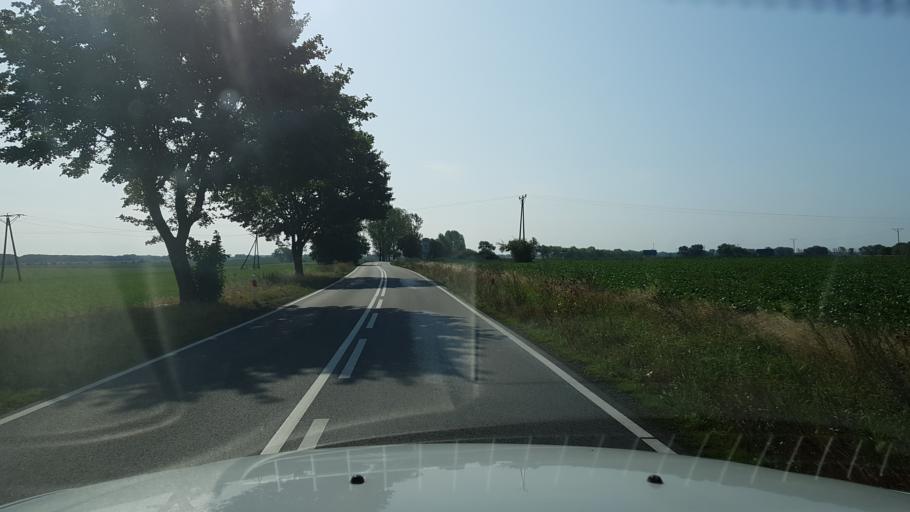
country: PL
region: West Pomeranian Voivodeship
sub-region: Powiat stargardzki
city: Stargard Szczecinski
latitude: 53.2645
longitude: 15.0930
